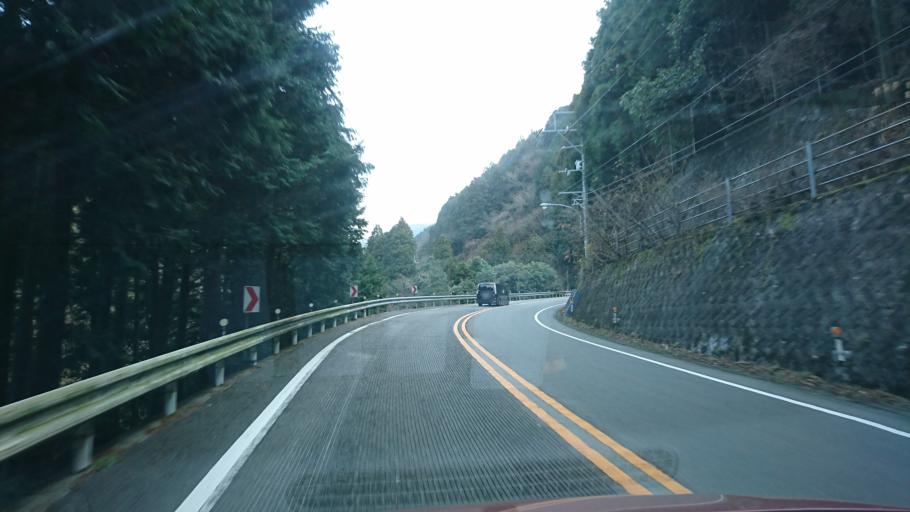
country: JP
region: Ehime
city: Hojo
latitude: 33.9655
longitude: 132.9057
